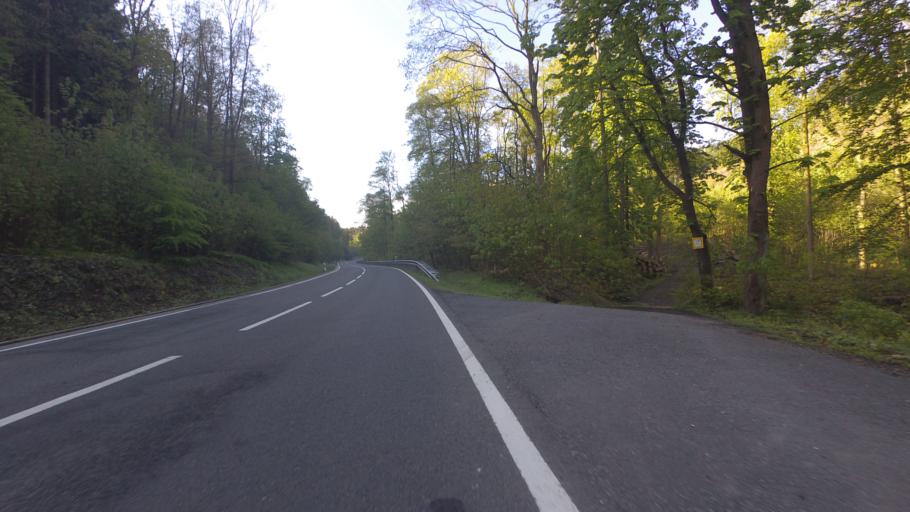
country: DE
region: Saxony-Anhalt
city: Darlingerode
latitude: 51.8058
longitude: 10.7315
